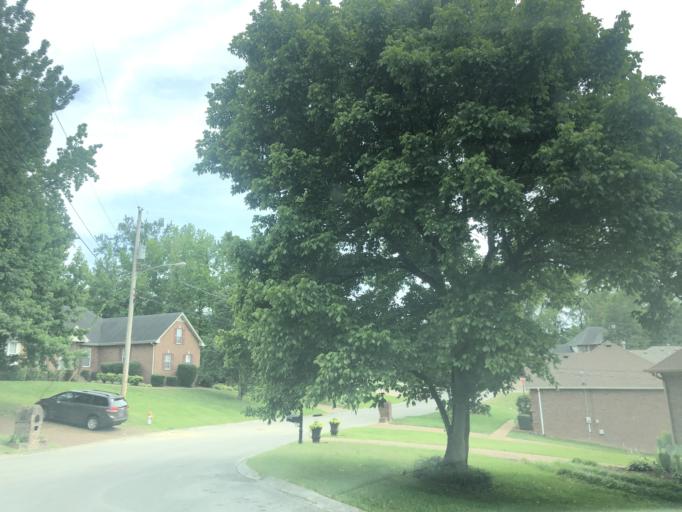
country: US
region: Tennessee
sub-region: Davidson County
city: Nashville
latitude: 36.2119
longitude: -86.8083
